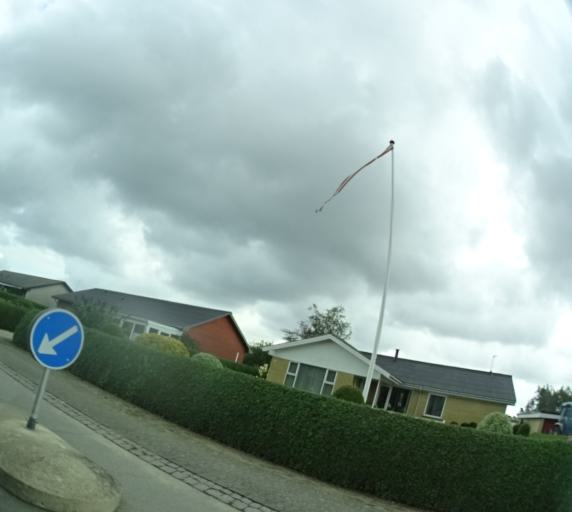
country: DK
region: Central Jutland
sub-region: Syddjurs Kommune
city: Ryomgard
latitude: 56.4094
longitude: 10.5755
